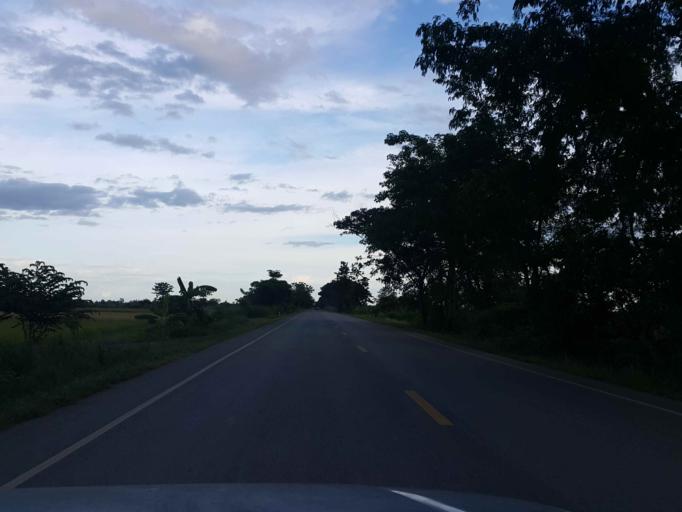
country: TH
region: Sukhothai
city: Sawankhalok
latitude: 17.3883
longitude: 99.7340
